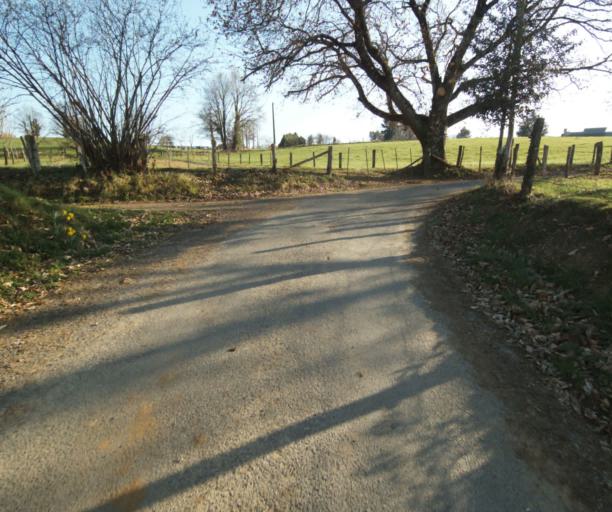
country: FR
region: Limousin
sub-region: Departement de la Correze
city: Saint-Clement
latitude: 45.3268
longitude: 1.6650
